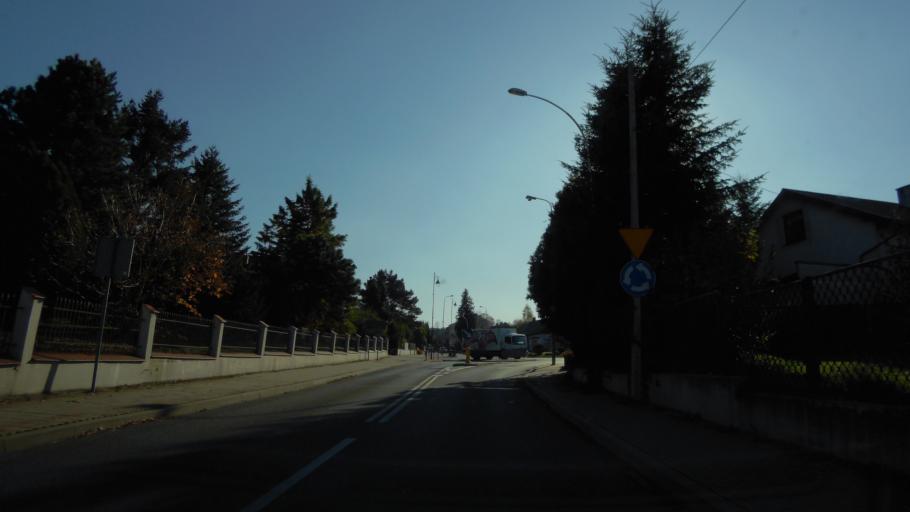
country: PL
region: Subcarpathian Voivodeship
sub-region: Powiat lezajski
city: Lezajsk
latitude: 50.2580
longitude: 22.4218
